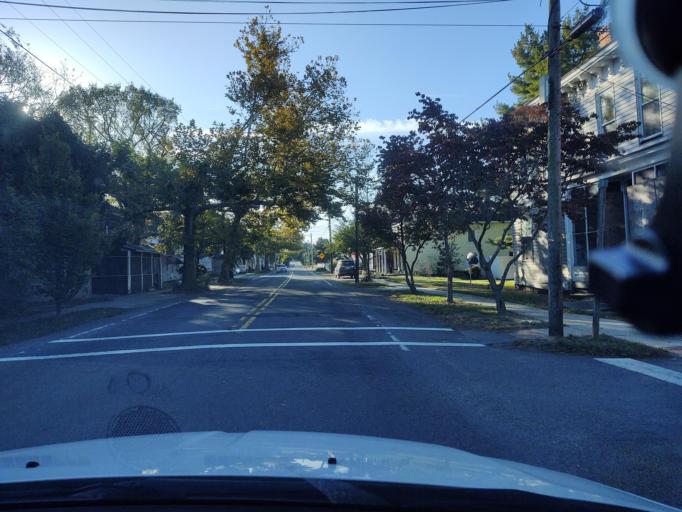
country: US
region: Maryland
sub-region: Queen Anne's County
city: Kingstown
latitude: 39.2418
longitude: -75.9227
